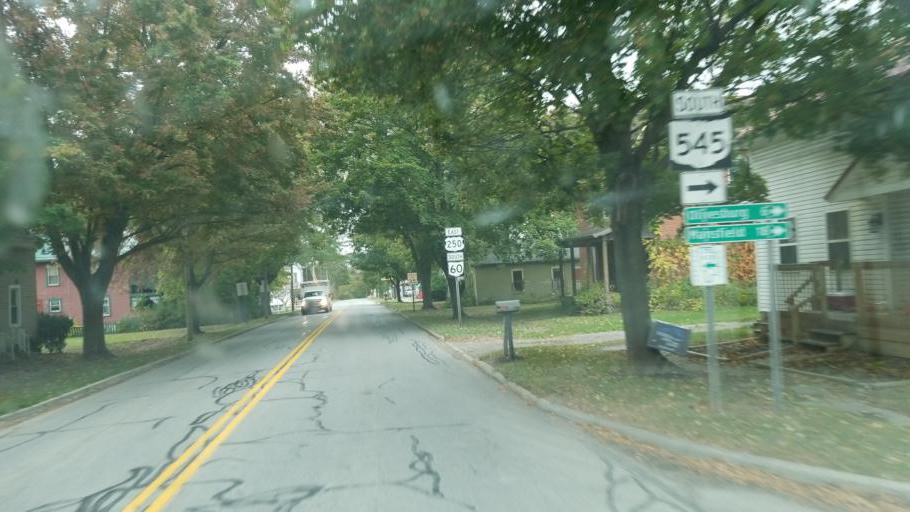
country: US
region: Ohio
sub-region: Ashland County
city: Ashland
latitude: 40.9666
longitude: -82.3647
